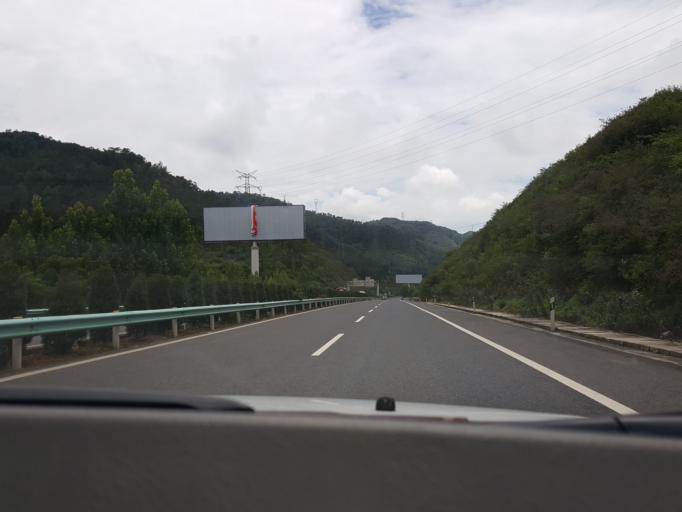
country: CN
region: Guangxi Zhuangzu Zizhiqu
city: Xinzhou
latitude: 25.1895
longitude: 105.0197
